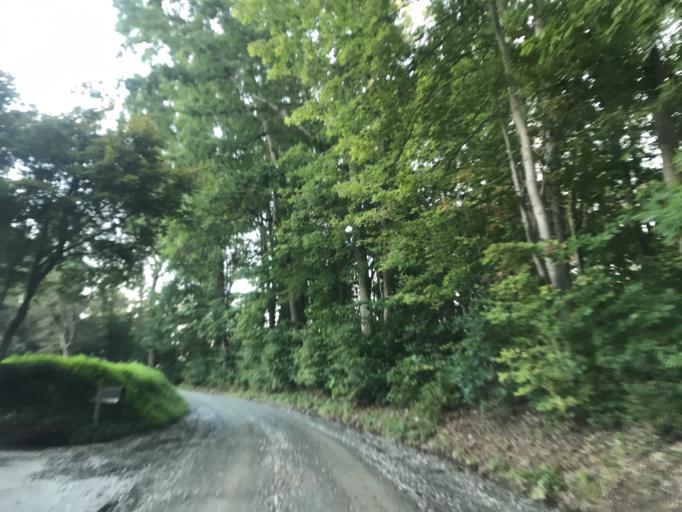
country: US
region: Maryland
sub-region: Harford County
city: Jarrettsville
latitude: 39.6705
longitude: -76.5334
